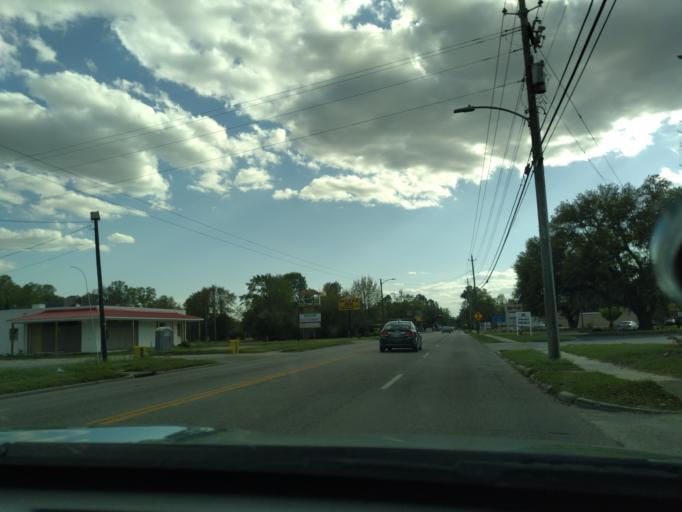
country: US
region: South Carolina
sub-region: Williamsburg County
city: Kingstree
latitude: 33.6802
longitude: -79.8277
